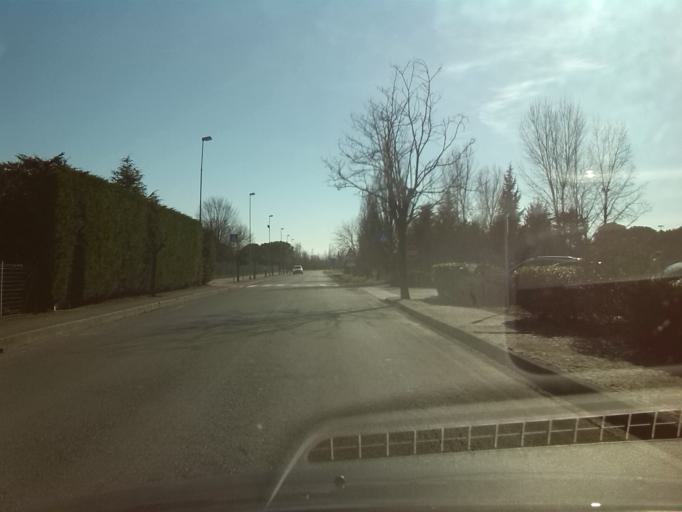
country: IT
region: Friuli Venezia Giulia
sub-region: Provincia di Udine
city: Povoletto
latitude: 46.1307
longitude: 13.2976
